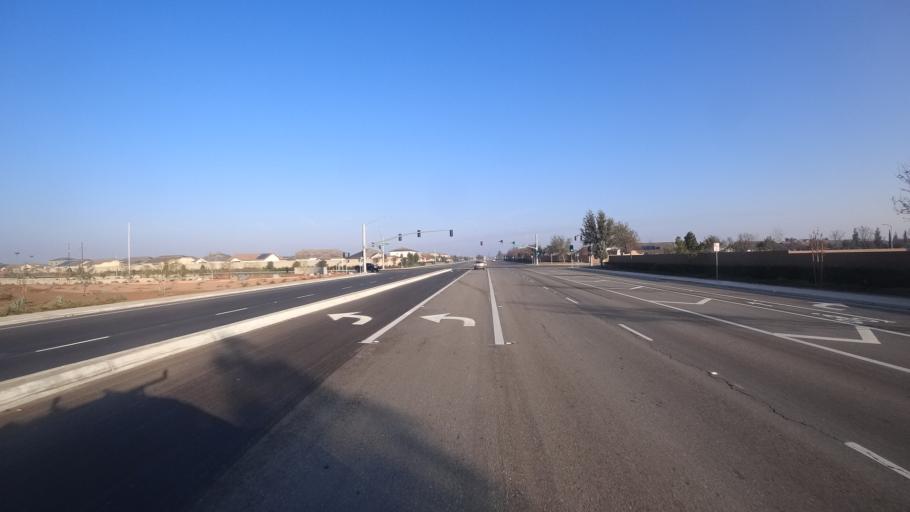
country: US
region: California
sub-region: Kern County
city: Greenacres
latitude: 35.2881
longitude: -119.1098
